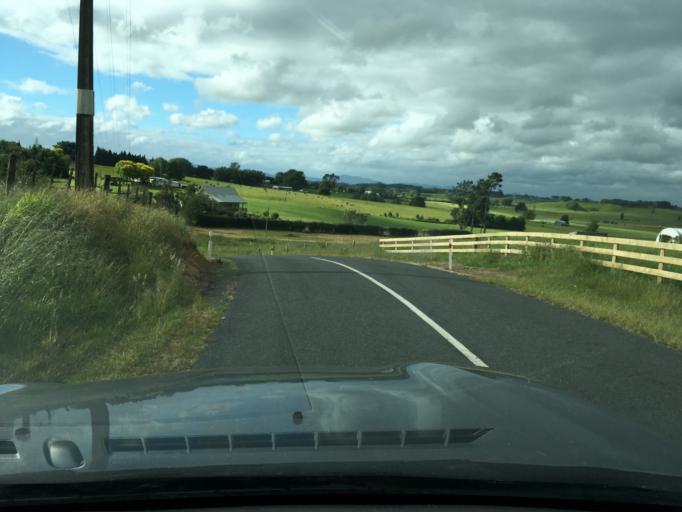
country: NZ
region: Waikato
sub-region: Hamilton City
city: Hamilton
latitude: -37.8283
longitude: 175.1799
